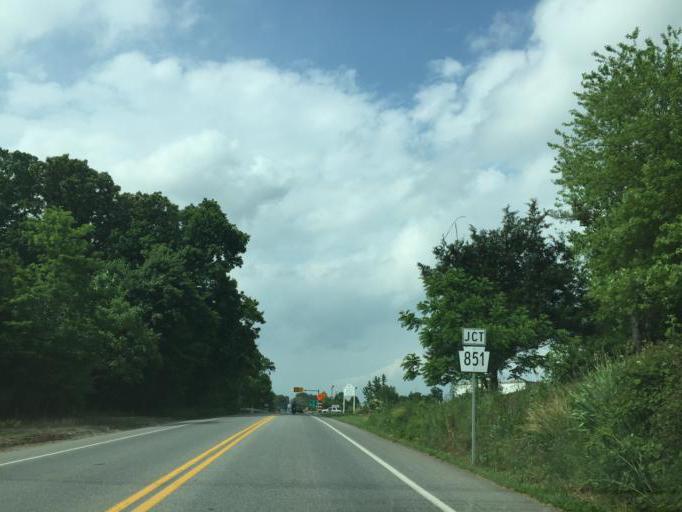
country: US
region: Pennsylvania
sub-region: York County
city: Susquehanna Trails
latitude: 39.7430
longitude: -76.3319
